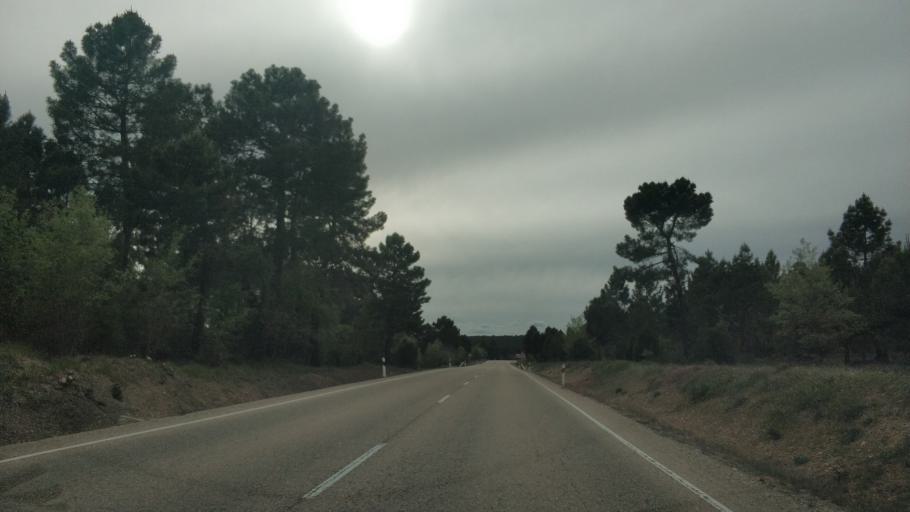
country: ES
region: Castille and Leon
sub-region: Provincia de Soria
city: Bayubas de Abajo
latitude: 41.5100
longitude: -2.9172
